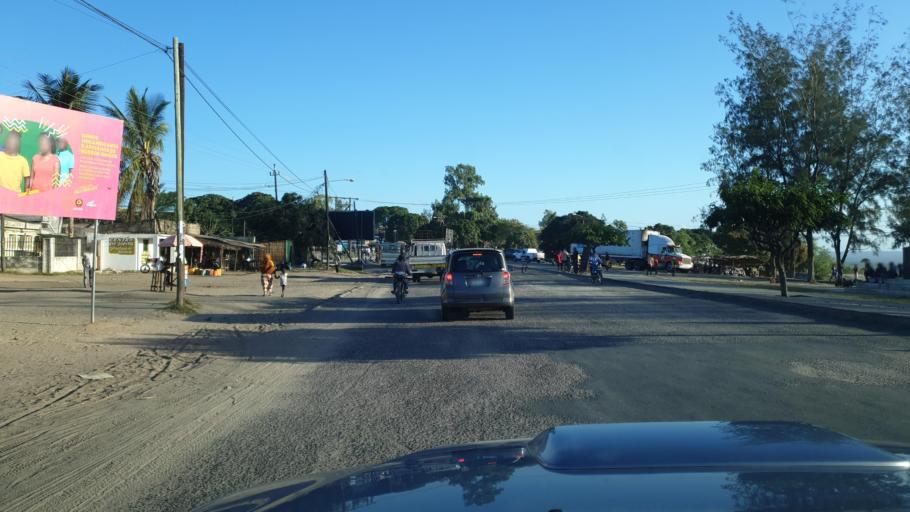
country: MZ
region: Nampula
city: Nacala
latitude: -14.5745
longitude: 40.6820
